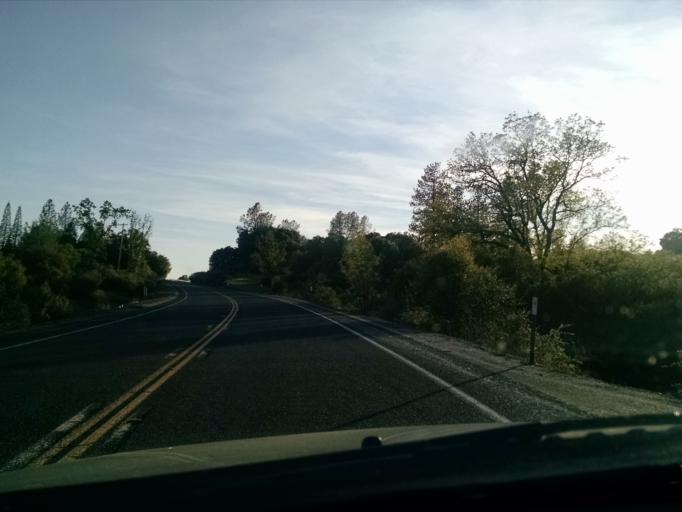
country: US
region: California
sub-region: Madera County
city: Ahwahnee
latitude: 37.4545
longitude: -119.8166
